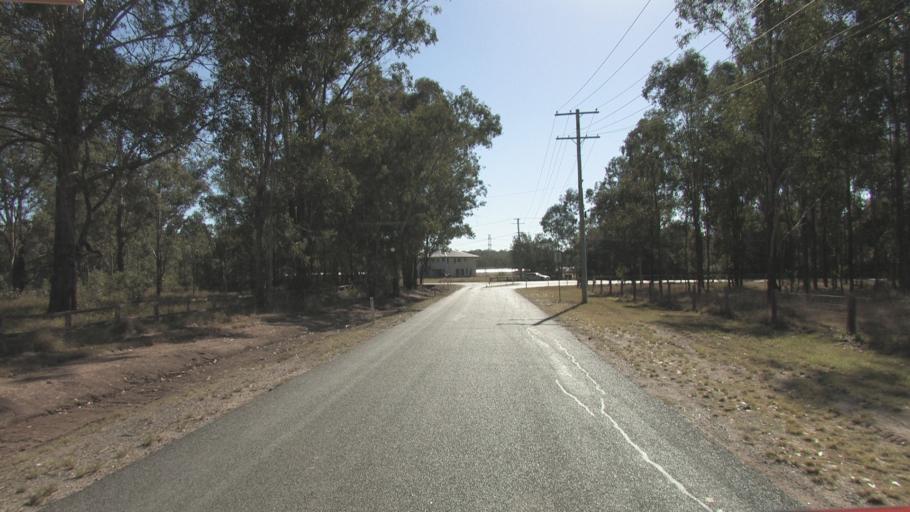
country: AU
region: Queensland
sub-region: Logan
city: Chambers Flat
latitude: -27.7506
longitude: 153.0767
